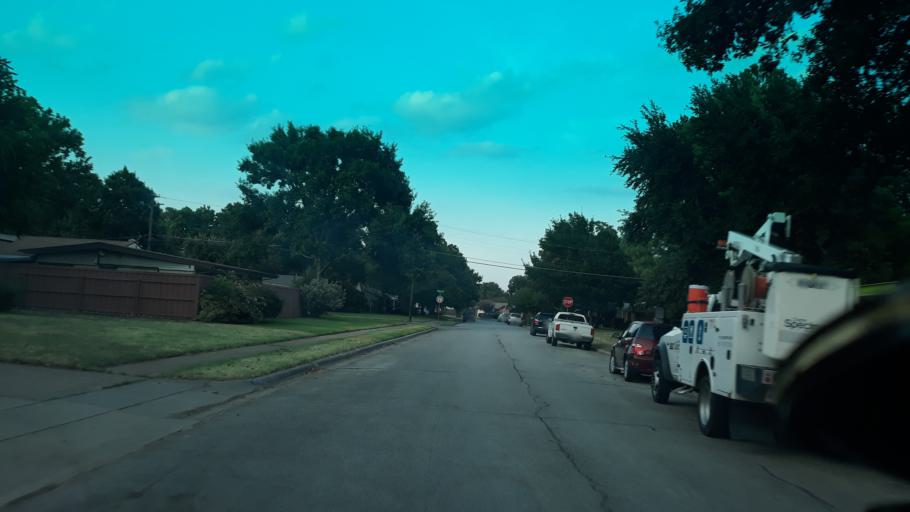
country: US
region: Texas
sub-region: Dallas County
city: Irving
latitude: 32.8347
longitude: -96.9821
